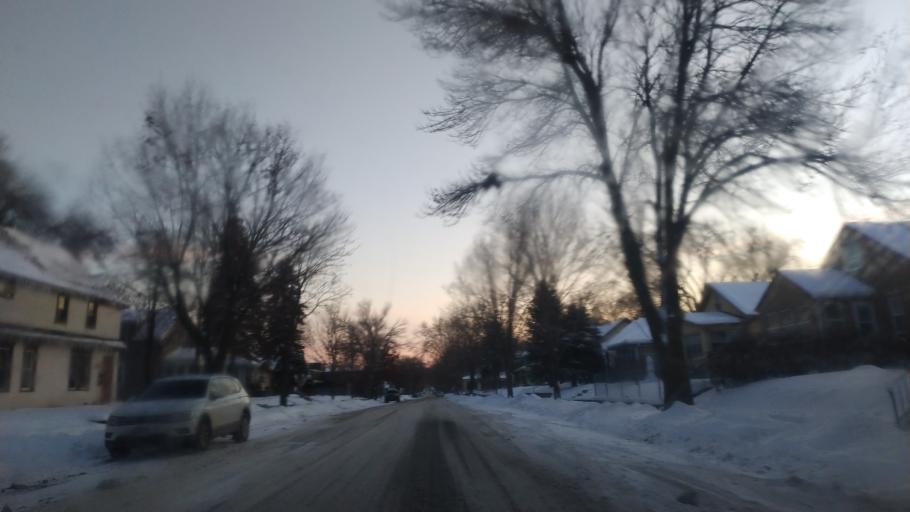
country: US
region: Minnesota
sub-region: Dakota County
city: South Saint Paul
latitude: 44.8905
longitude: -93.0463
